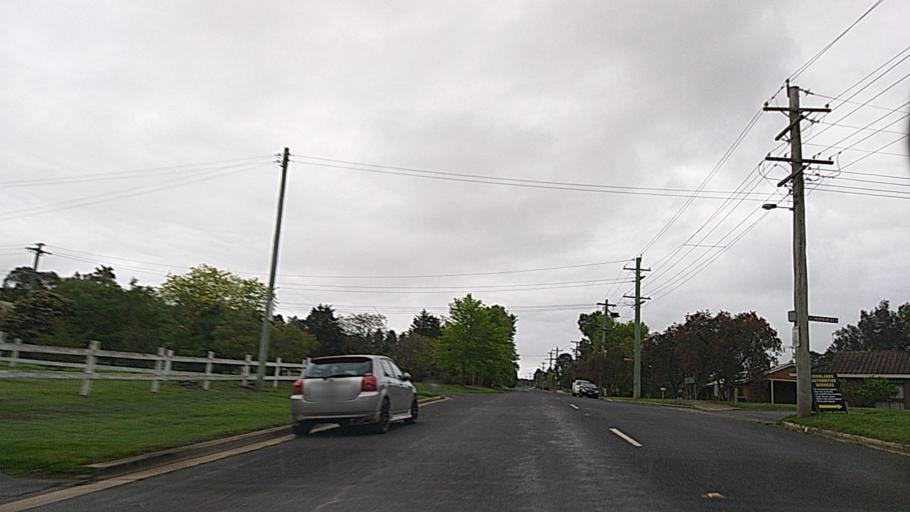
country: AU
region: New South Wales
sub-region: Wollondilly
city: Douglas Park
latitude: -34.1806
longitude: 150.7117
